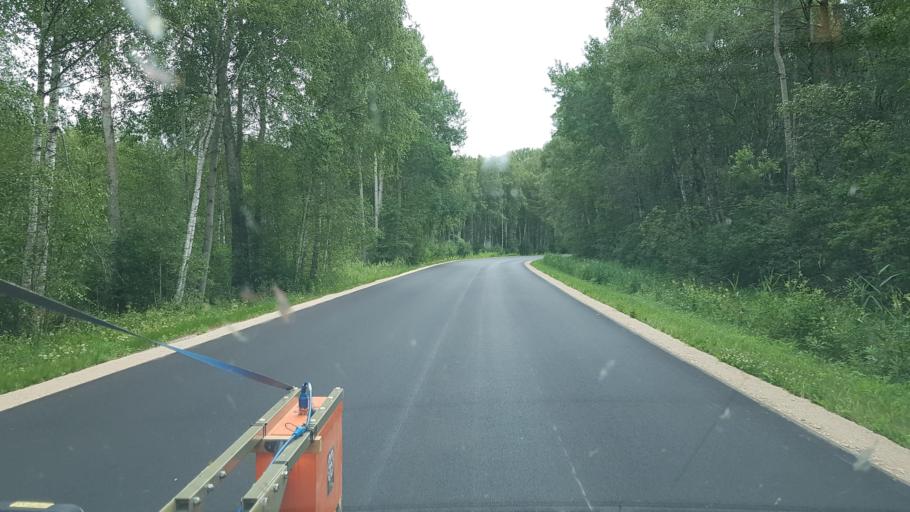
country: EE
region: Paernumaa
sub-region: Audru vald
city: Audru
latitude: 58.6246
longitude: 24.2594
